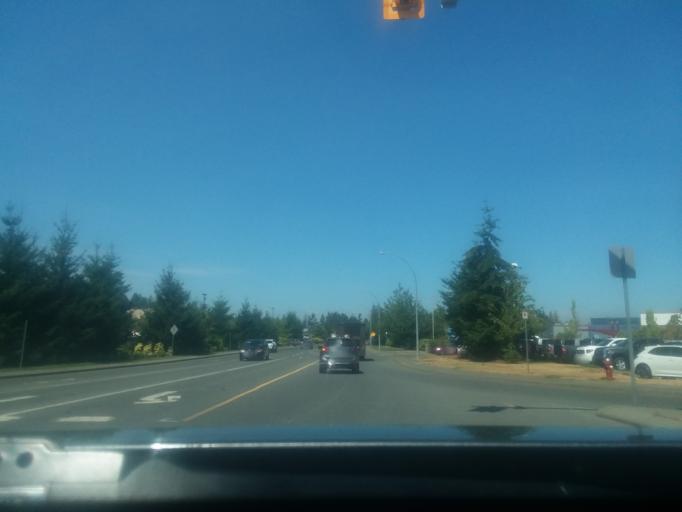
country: CA
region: British Columbia
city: Courtenay
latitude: 49.7129
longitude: -124.9613
